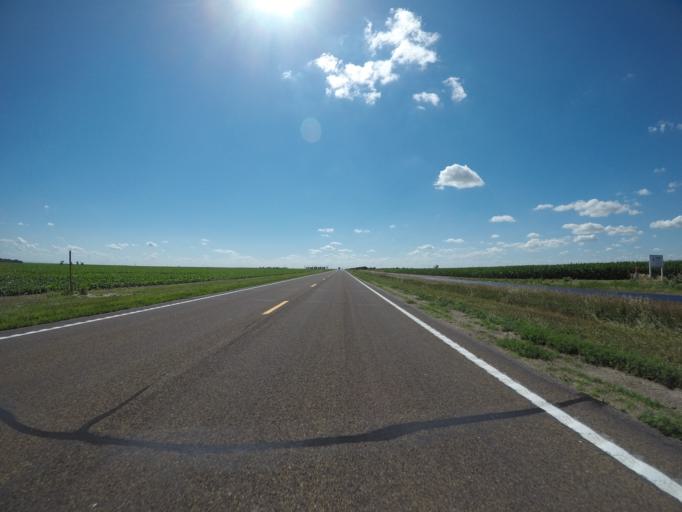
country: US
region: Nebraska
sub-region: Chase County
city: Imperial
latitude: 40.5377
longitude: -101.8880
